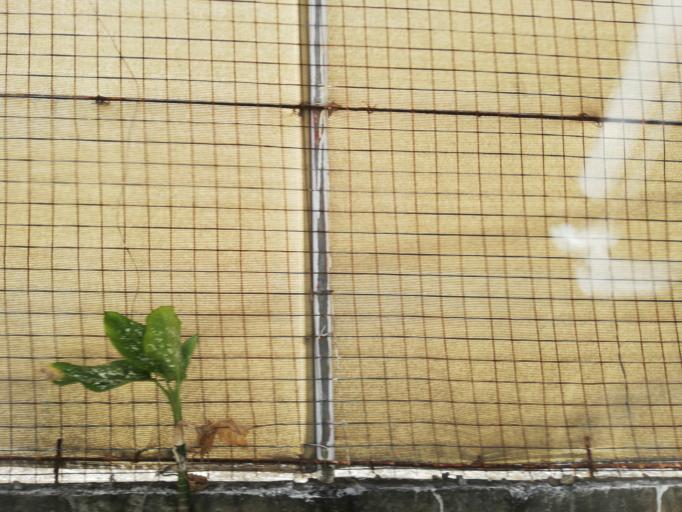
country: MU
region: Moka
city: Moka
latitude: -20.2213
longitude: 57.4654
